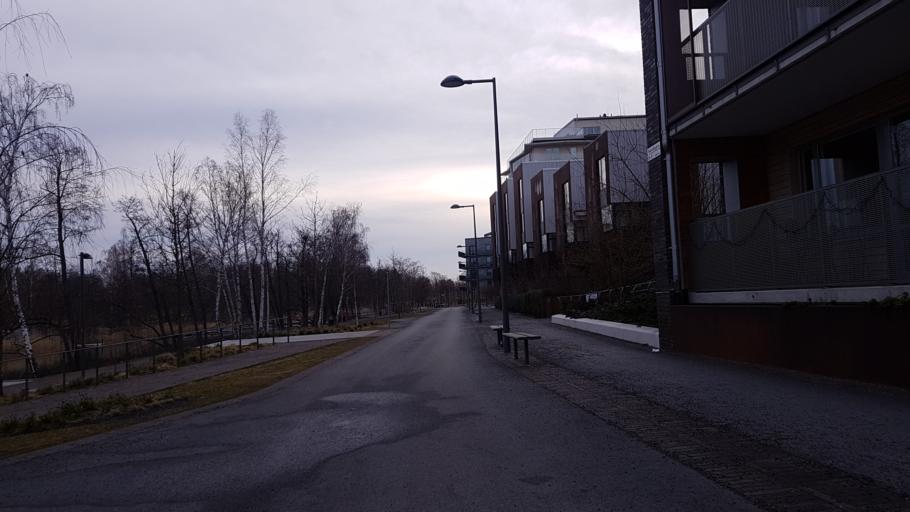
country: SE
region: Stockholm
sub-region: Stockholms Kommun
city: OEstermalm
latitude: 59.3594
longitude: 18.0897
